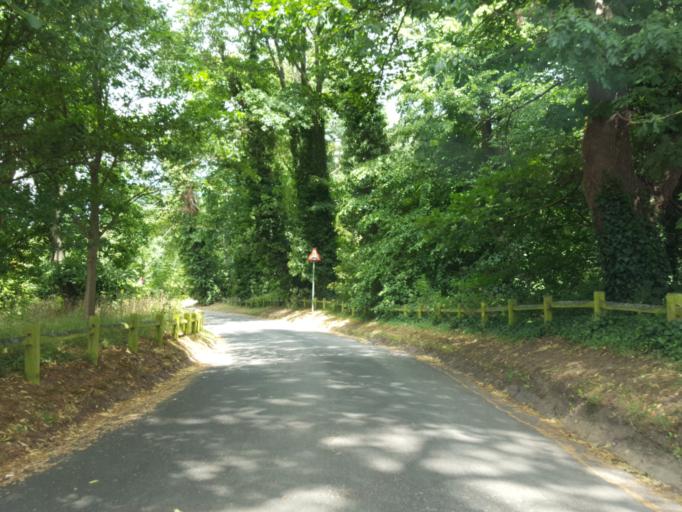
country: GB
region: England
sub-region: Kent
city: Boxley
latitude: 51.2868
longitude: 0.5394
